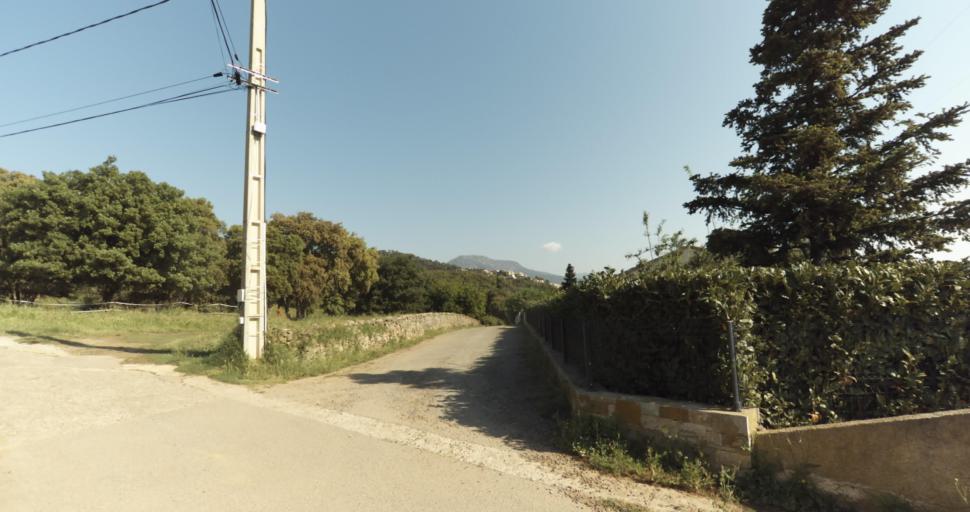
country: FR
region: Corsica
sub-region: Departement de la Haute-Corse
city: Biguglia
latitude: 42.6310
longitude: 9.4245
